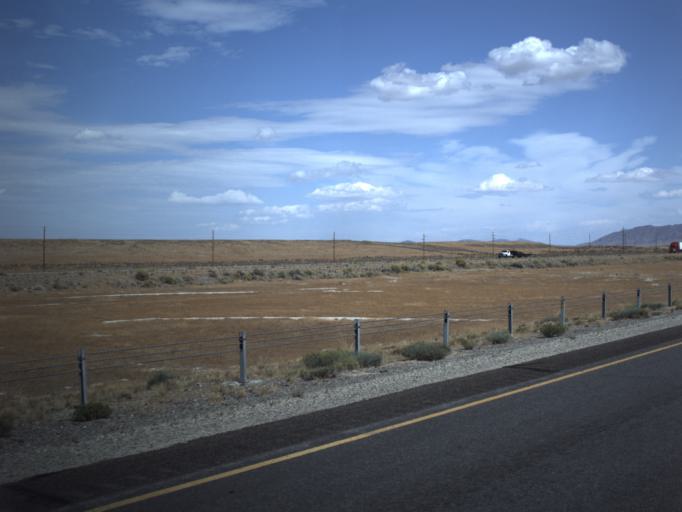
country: US
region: Utah
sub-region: Tooele County
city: Grantsville
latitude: 40.7251
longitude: -113.1502
